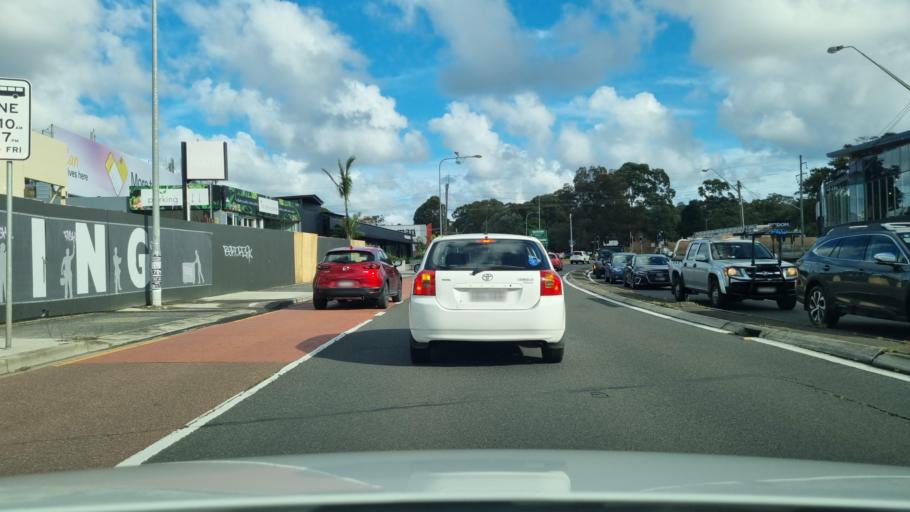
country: AU
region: New South Wales
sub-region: Manly Vale
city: Fairlight
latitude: -33.7874
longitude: 151.2665
